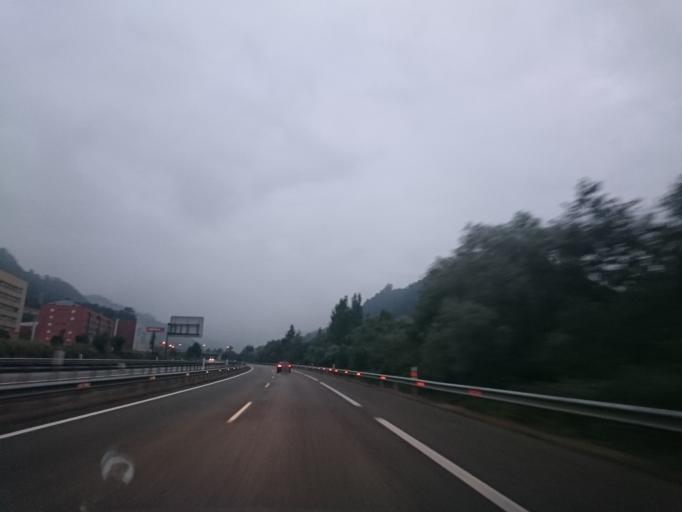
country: ES
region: Asturias
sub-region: Province of Asturias
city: Mieres
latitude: 43.2277
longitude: -5.7834
